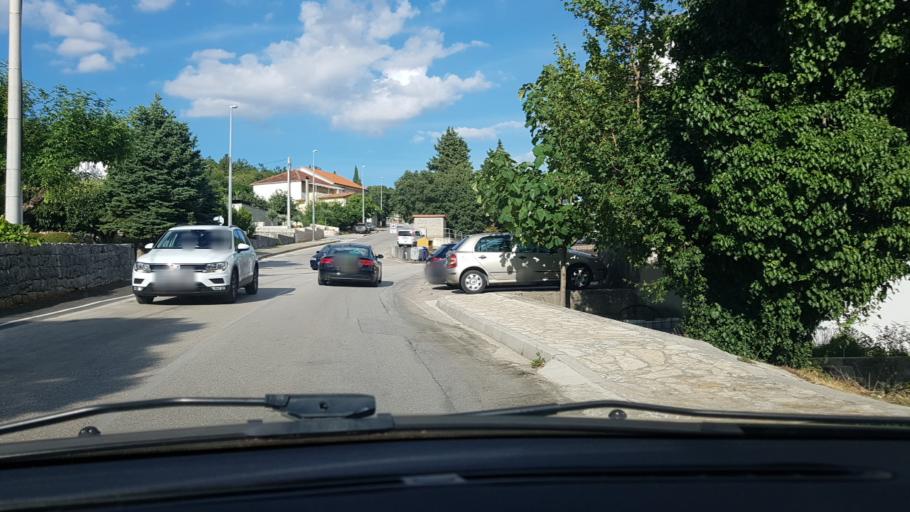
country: HR
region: Splitsko-Dalmatinska
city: Imotski
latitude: 43.4457
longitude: 17.2030
